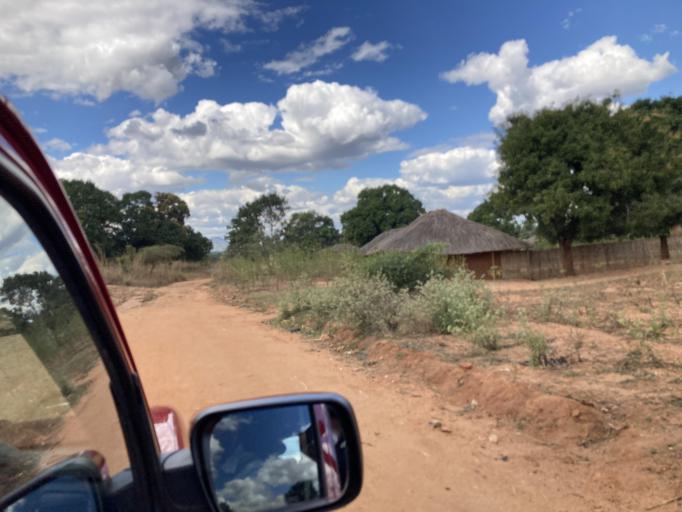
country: MZ
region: Cabo Delgado
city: Montepuez
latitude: -13.1266
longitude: 39.0345
